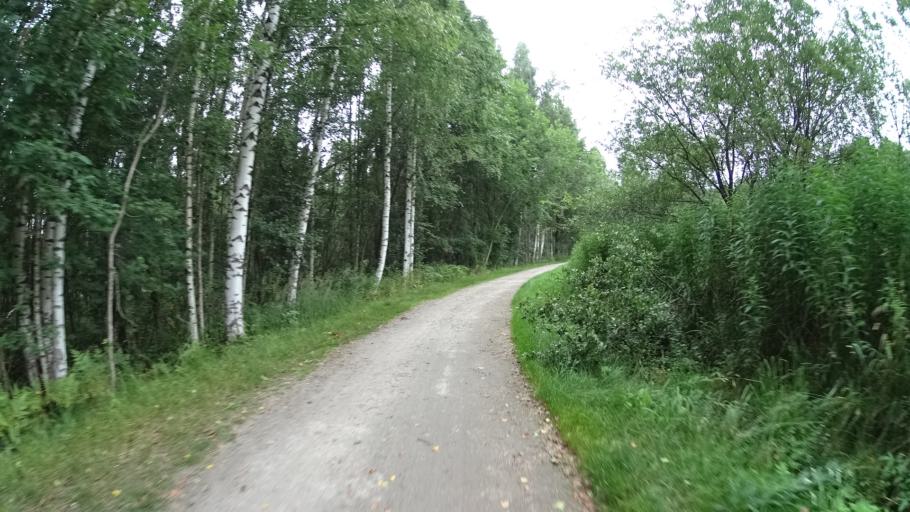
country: FI
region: Uusimaa
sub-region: Helsinki
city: Teekkarikylae
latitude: 60.2114
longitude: 24.8428
